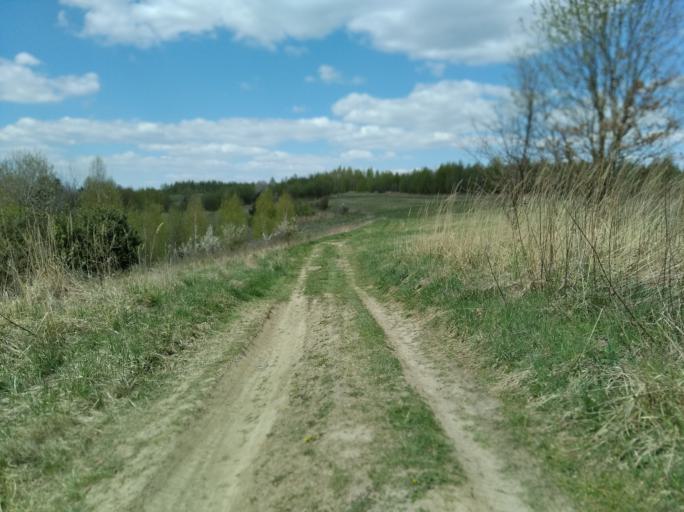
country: PL
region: Subcarpathian Voivodeship
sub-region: Powiat brzozowski
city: Wesola
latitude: 49.7505
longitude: 22.0775
